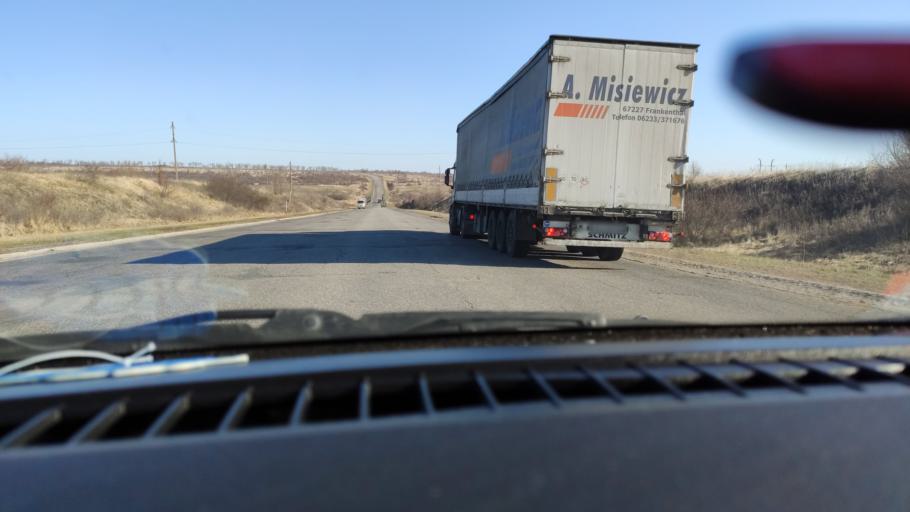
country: RU
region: Samara
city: Varlamovo
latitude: 53.0905
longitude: 48.3553
